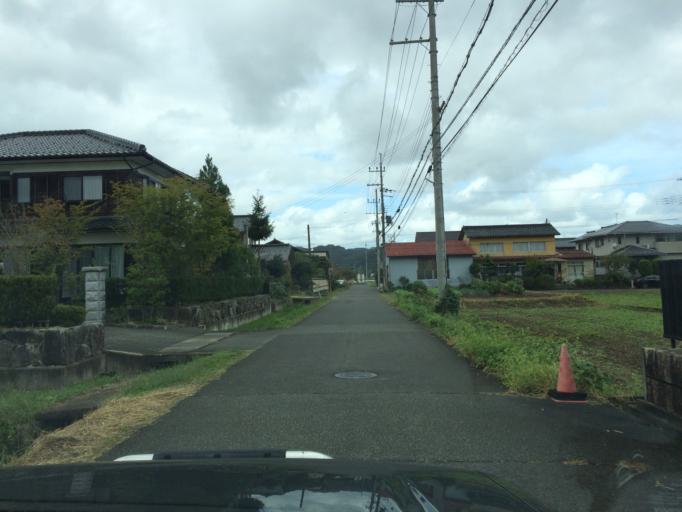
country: JP
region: Hyogo
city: Toyooka
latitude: 35.4786
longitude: 134.7855
